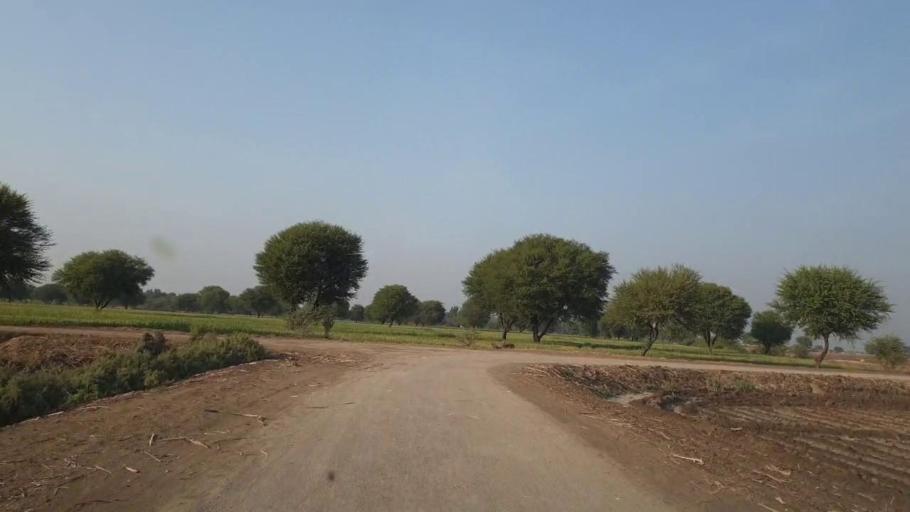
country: PK
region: Sindh
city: Pithoro
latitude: 25.6735
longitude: 69.2036
